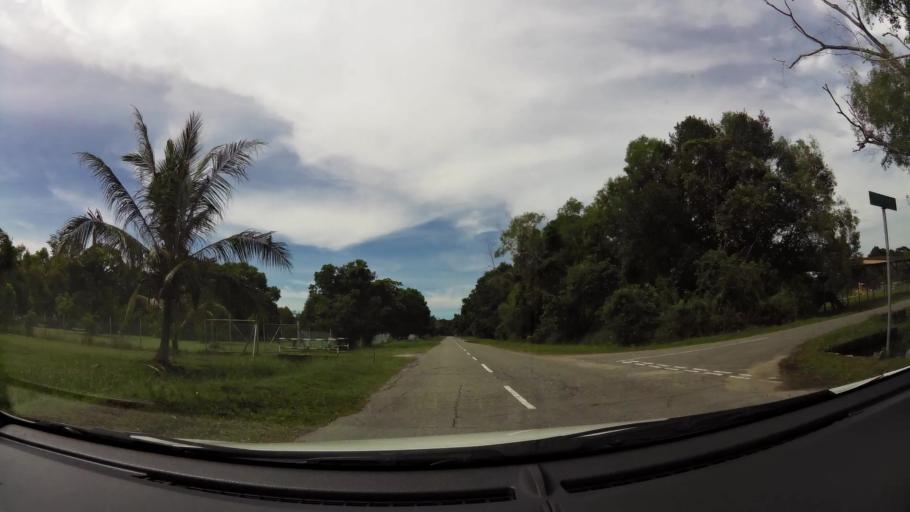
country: BN
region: Belait
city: Seria
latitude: 4.6047
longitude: 114.3009
